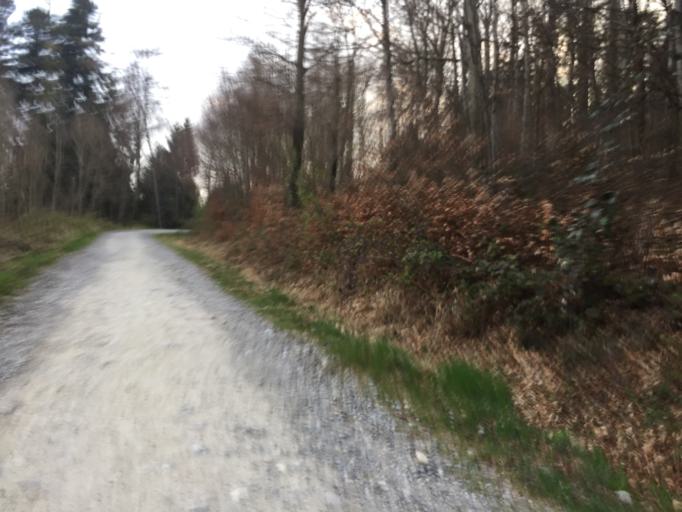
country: CH
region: Bern
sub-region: Bern-Mittelland District
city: Koniz
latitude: 46.9185
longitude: 7.4324
